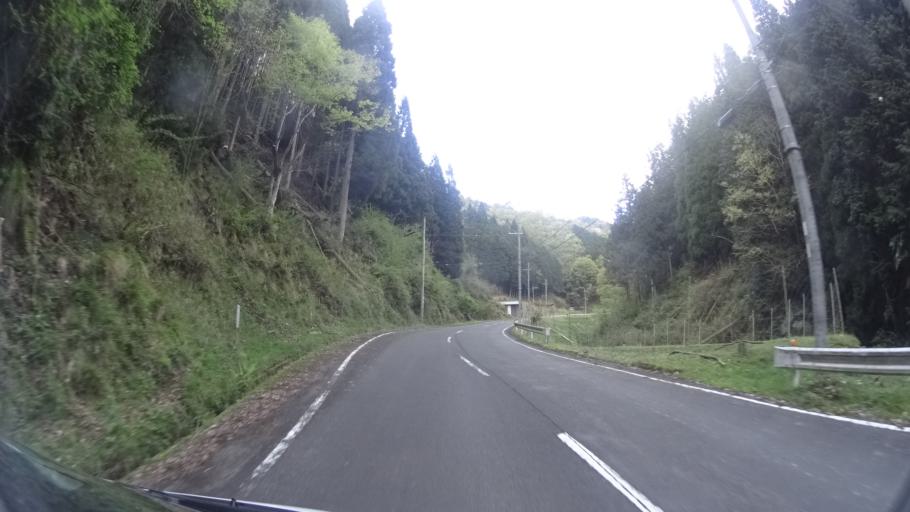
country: JP
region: Kyoto
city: Ayabe
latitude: 35.2546
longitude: 135.3135
